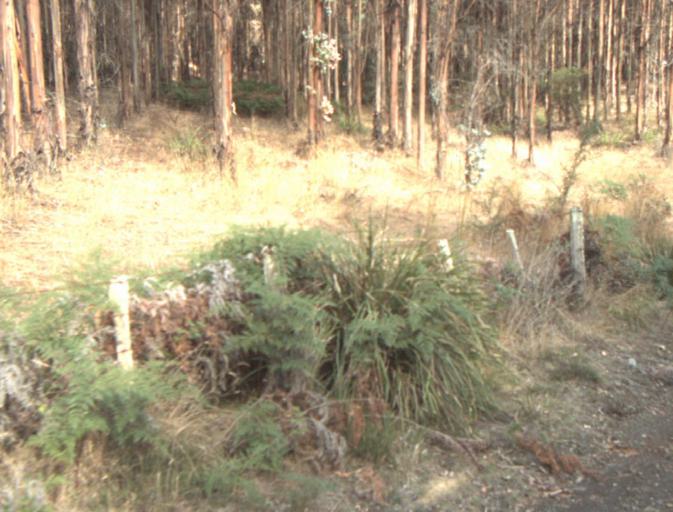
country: AU
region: Tasmania
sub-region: Launceston
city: Mayfield
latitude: -41.2151
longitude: 147.1773
